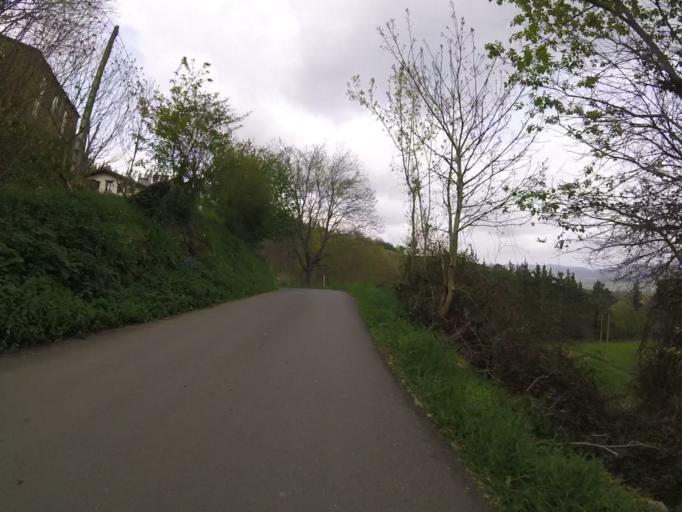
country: ES
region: Basque Country
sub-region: Provincia de Guipuzcoa
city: Anoeta
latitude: 43.1737
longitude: -2.0828
